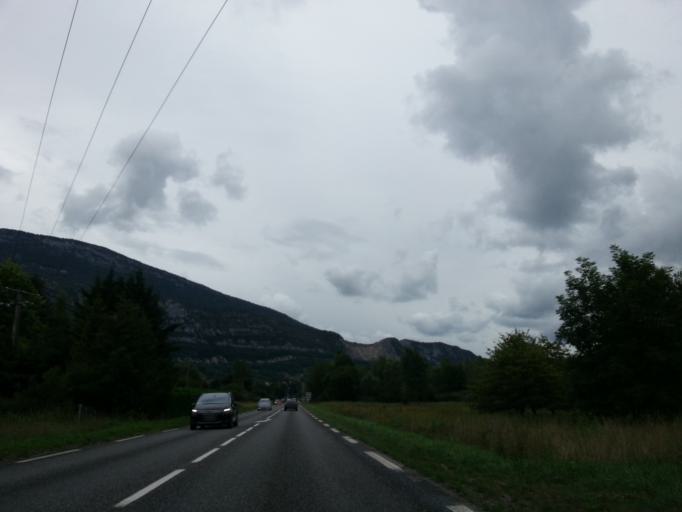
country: FR
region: Rhone-Alpes
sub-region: Departement de la Haute-Savoie
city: Doussard
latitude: 45.7862
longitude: 6.2221
